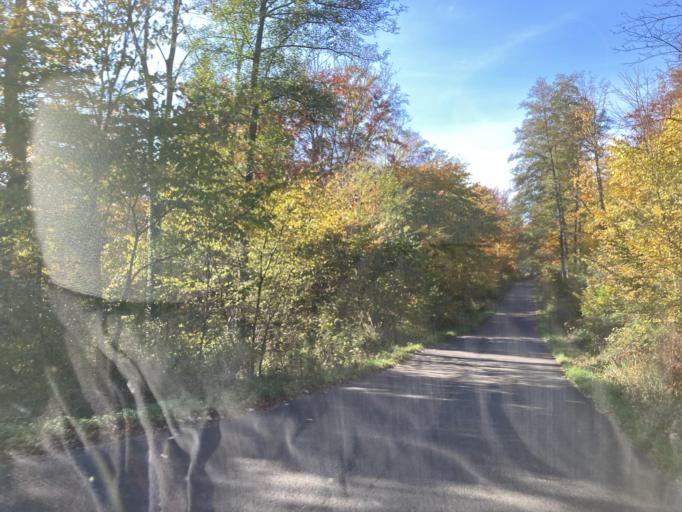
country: DE
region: Baden-Wuerttemberg
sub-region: Tuebingen Region
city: Mossingen
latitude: 48.3822
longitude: 9.0683
